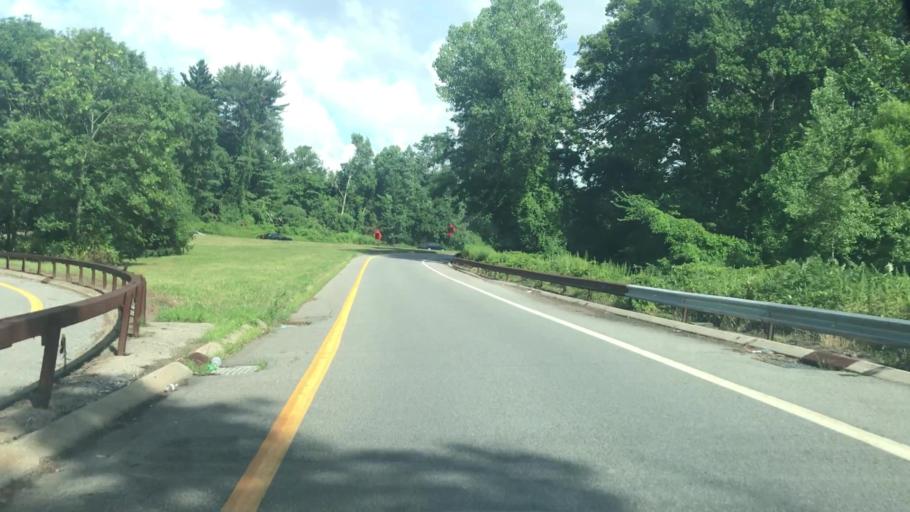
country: US
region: New York
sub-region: Westchester County
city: Tuckahoe
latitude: 40.9532
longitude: -73.8005
